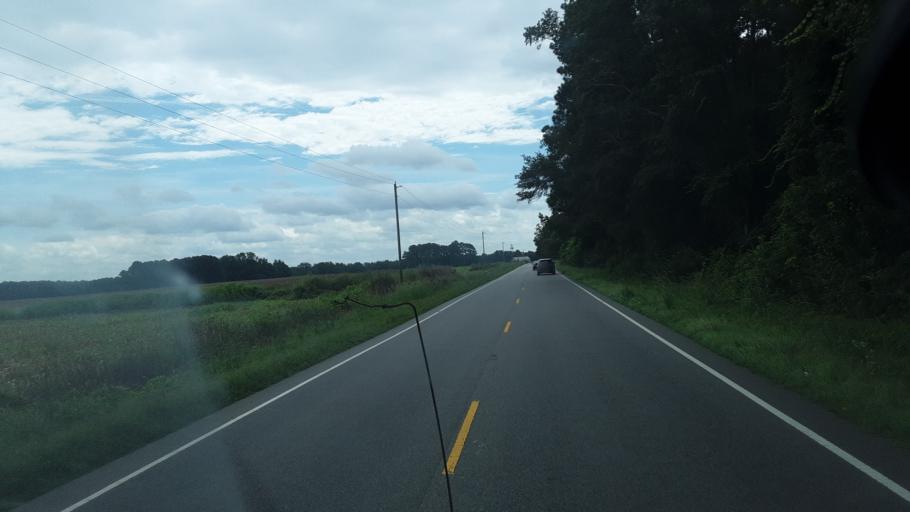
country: US
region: North Carolina
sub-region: Robeson County
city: Rowland
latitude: 34.6022
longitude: -79.3298
